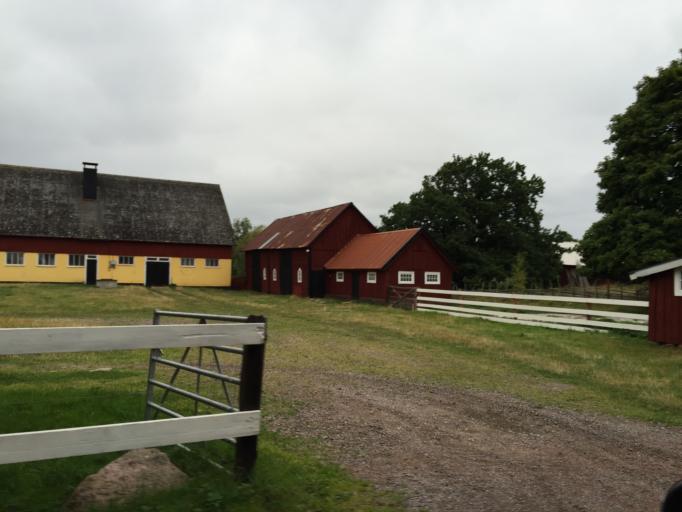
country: SE
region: Kalmar
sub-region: Monsteras Kommun
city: Moensteras
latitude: 57.0478
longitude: 16.5604
